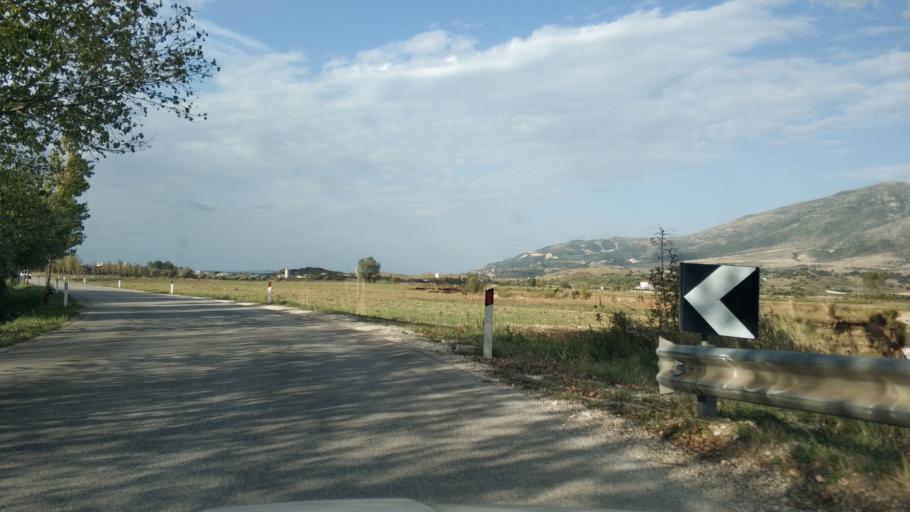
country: AL
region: Vlore
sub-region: Rrethi i Vlores
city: Orikum
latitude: 40.3145
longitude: 19.4860
